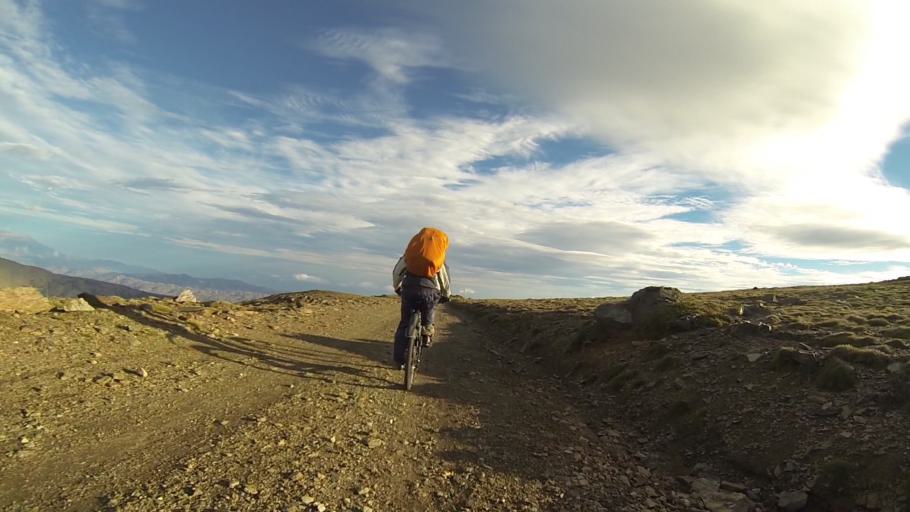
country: ES
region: Andalusia
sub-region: Provincia de Granada
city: Trevelez
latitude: 37.0115
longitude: -3.3032
